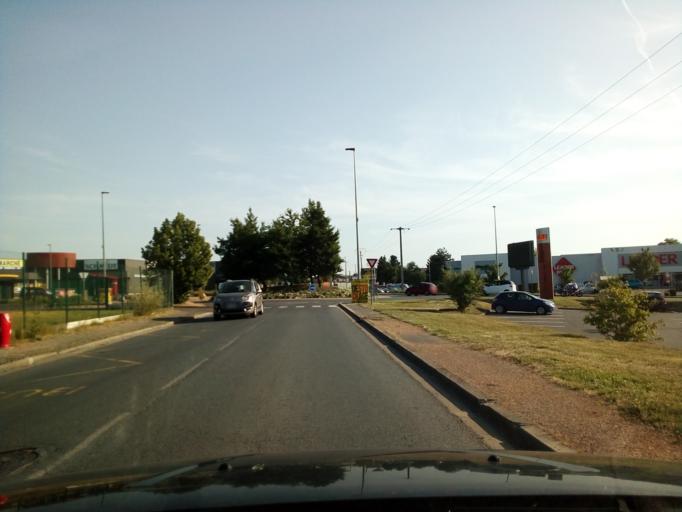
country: FR
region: Auvergne
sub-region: Departement de l'Allier
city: Domerat
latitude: 46.3673
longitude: 2.5684
